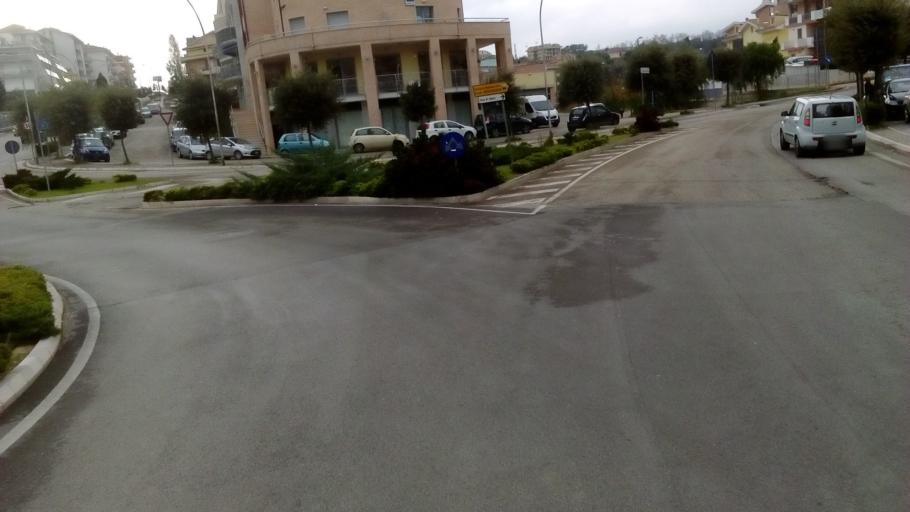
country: IT
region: Abruzzo
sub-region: Provincia di Chieti
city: Vasto
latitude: 42.1076
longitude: 14.7022
